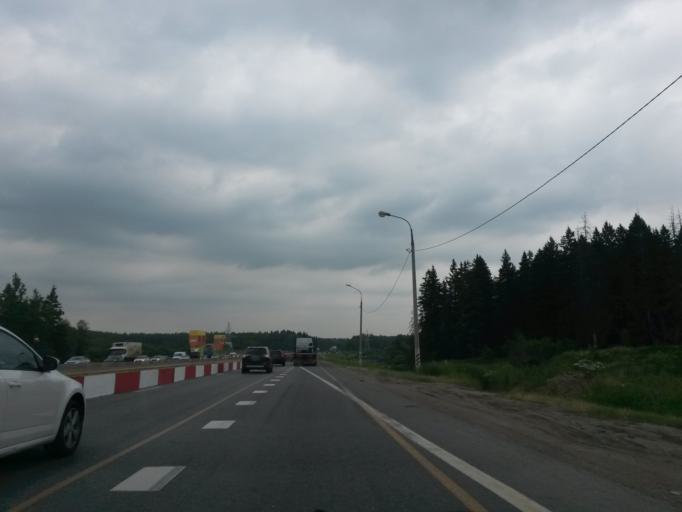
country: RU
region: Moskovskaya
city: Lyubuchany
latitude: 55.2311
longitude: 37.5294
